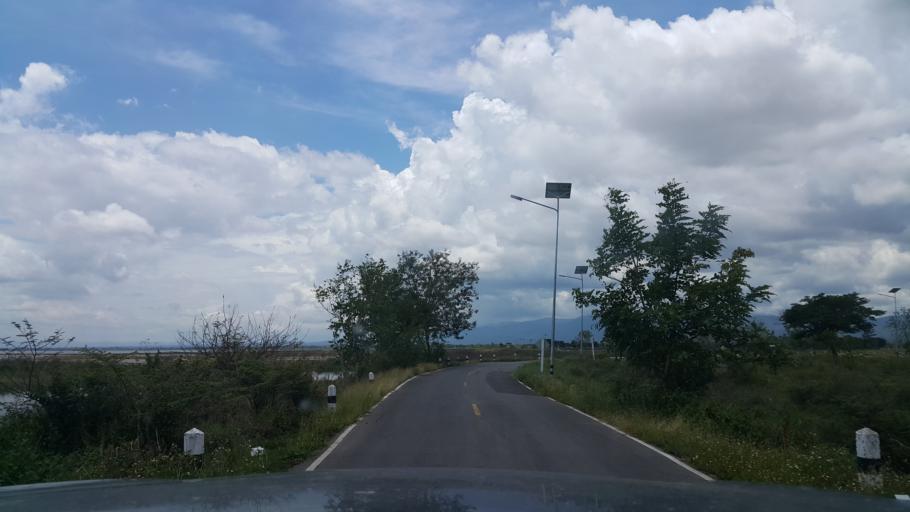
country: TH
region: Phayao
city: Phayao
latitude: 19.1858
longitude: 99.8556
